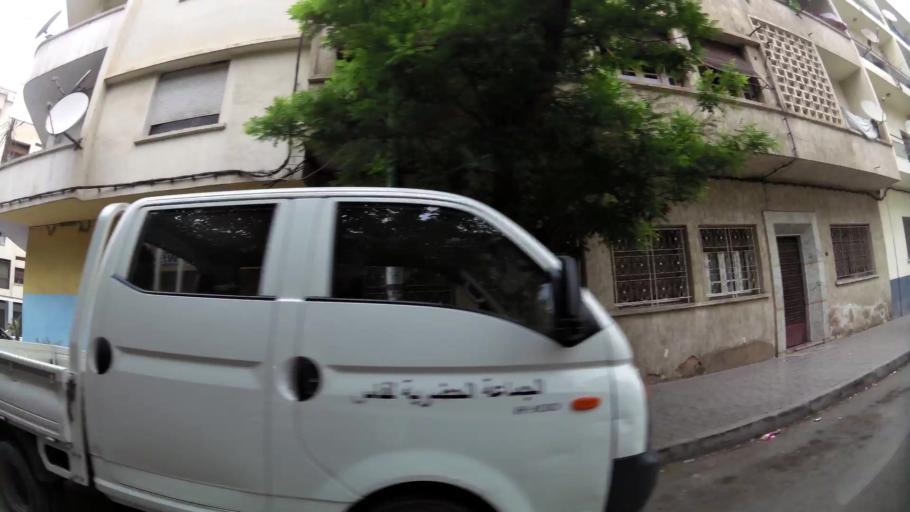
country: MA
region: Fes-Boulemane
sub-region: Fes
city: Fes
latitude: 34.0446
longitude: -5.0052
